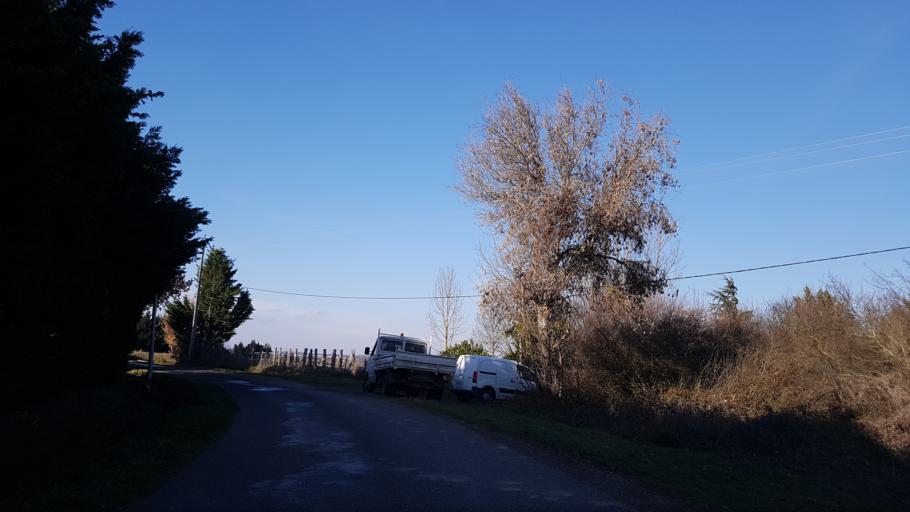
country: FR
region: Midi-Pyrenees
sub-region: Departement de l'Ariege
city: La Tour-du-Crieu
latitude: 43.1623
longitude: 1.6807
